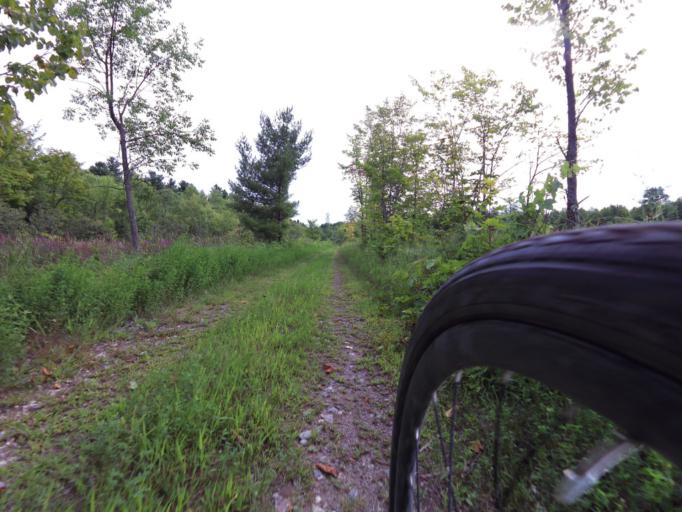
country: CA
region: Ontario
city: Gananoque
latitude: 44.6048
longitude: -76.2860
